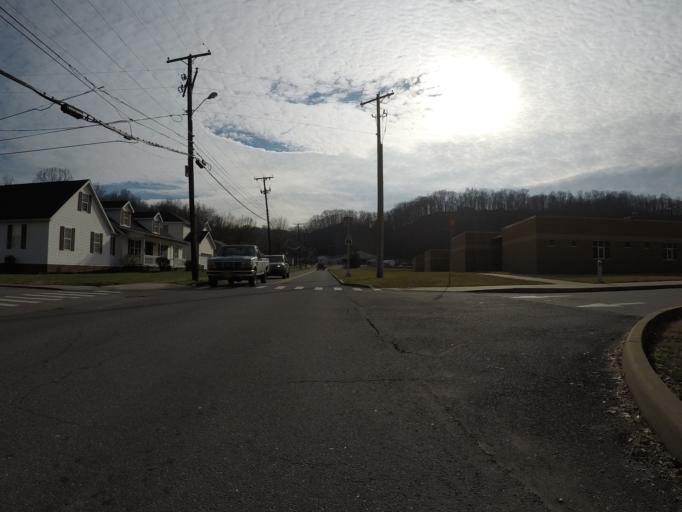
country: US
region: West Virginia
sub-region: Cabell County
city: Barboursville
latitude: 38.4033
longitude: -82.2935
